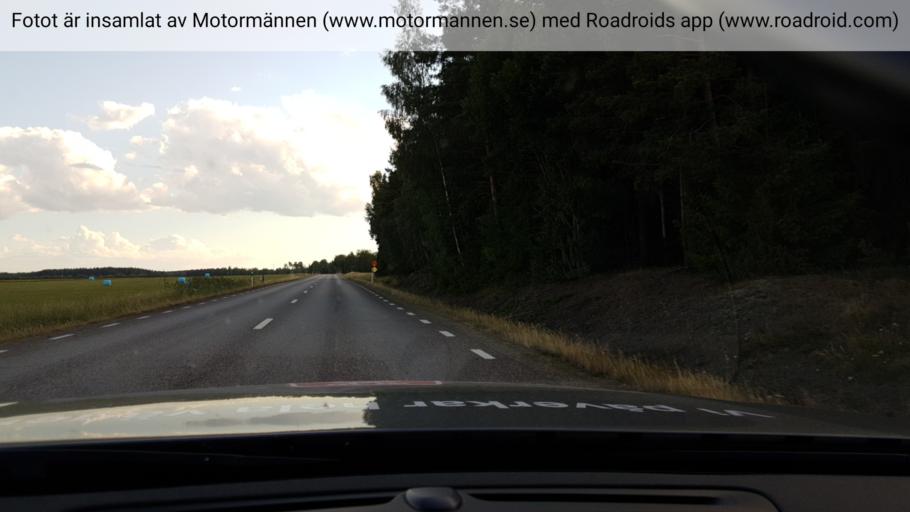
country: SE
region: Uppsala
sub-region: Enkopings Kommun
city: Irsta
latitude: 59.8080
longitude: 16.9154
